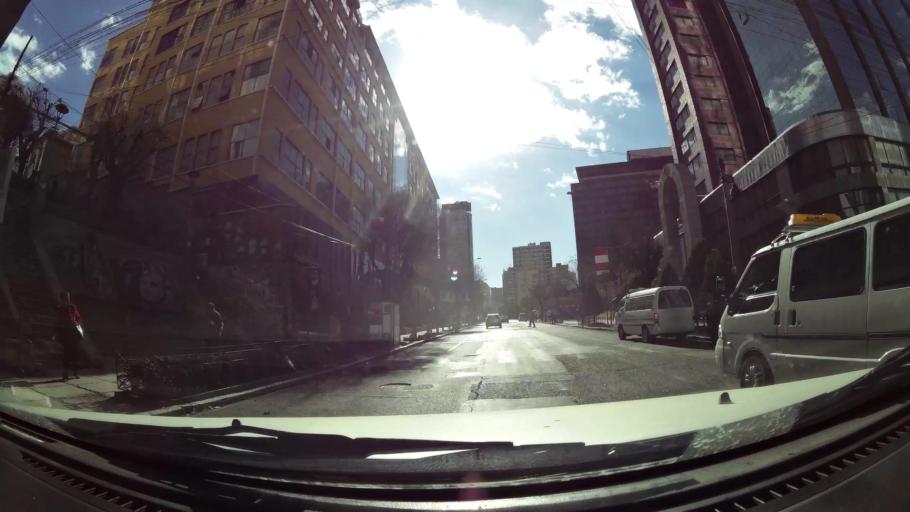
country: BO
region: La Paz
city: La Paz
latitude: -16.5077
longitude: -68.1263
